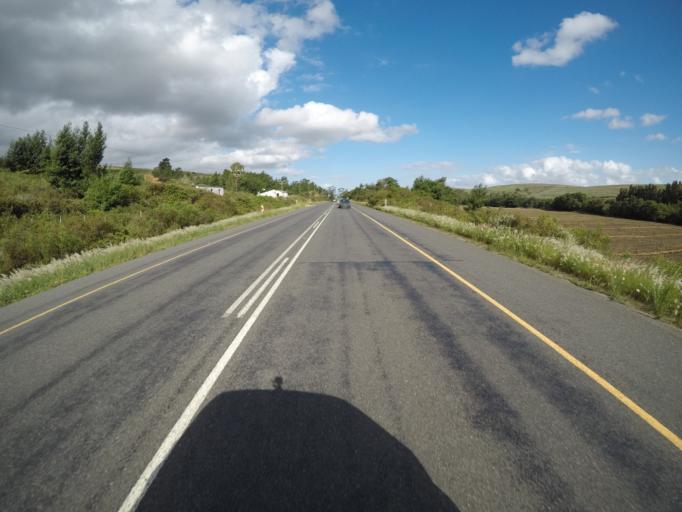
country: ZA
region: Western Cape
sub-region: Overberg District Municipality
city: Swellendam
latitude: -34.0060
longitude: 20.3804
